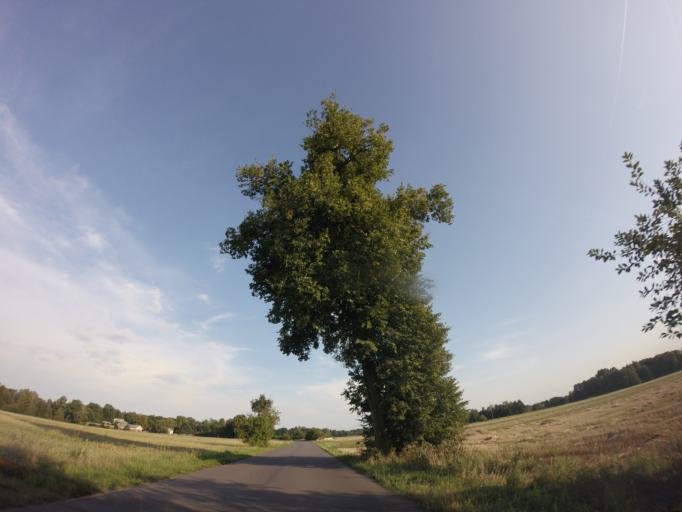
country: PL
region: Lublin Voivodeship
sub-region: Powiat pulawski
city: Kurow
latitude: 51.4279
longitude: 22.2179
